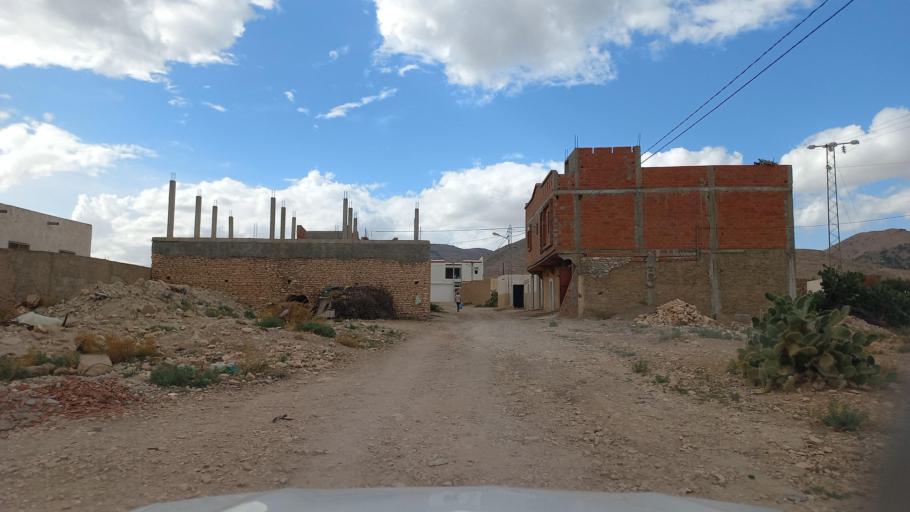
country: TN
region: Al Qasrayn
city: Sbiba
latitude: 35.4466
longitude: 9.0786
